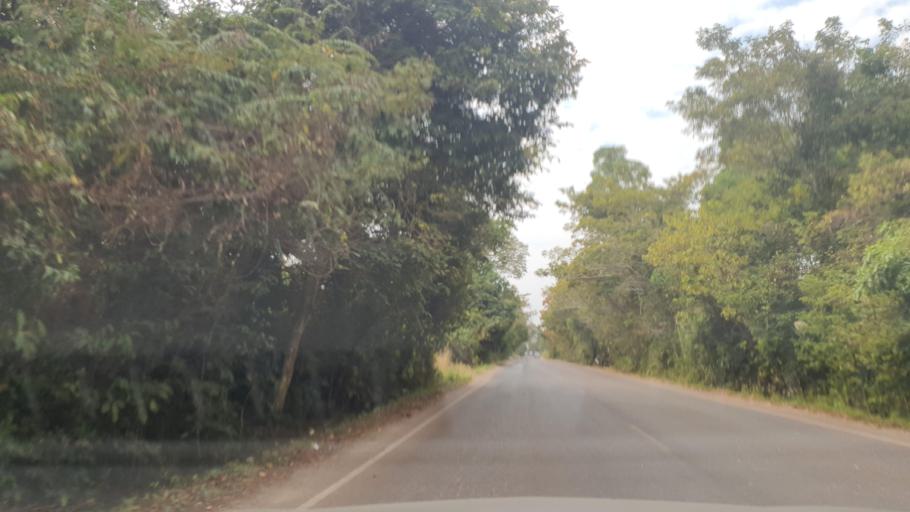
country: TH
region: Changwat Bueng Kan
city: Bung Khla
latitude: 18.3020
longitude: 103.9544
